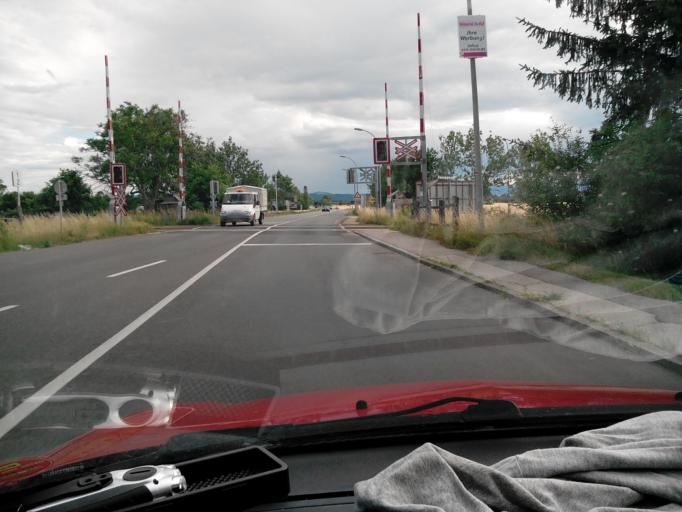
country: AT
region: Lower Austria
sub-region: Wiener Neustadt Stadt
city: Wiener Neustadt
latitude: 47.7981
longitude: 16.2394
